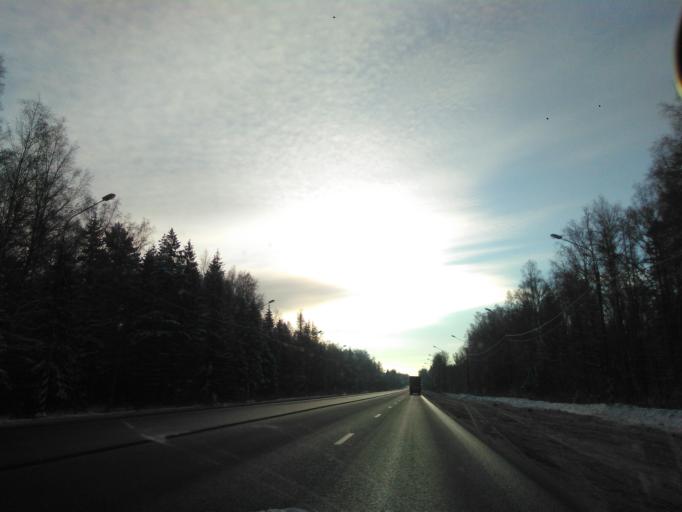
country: RU
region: Moskovskaya
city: Reshetnikovo
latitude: 56.4504
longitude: 36.6024
